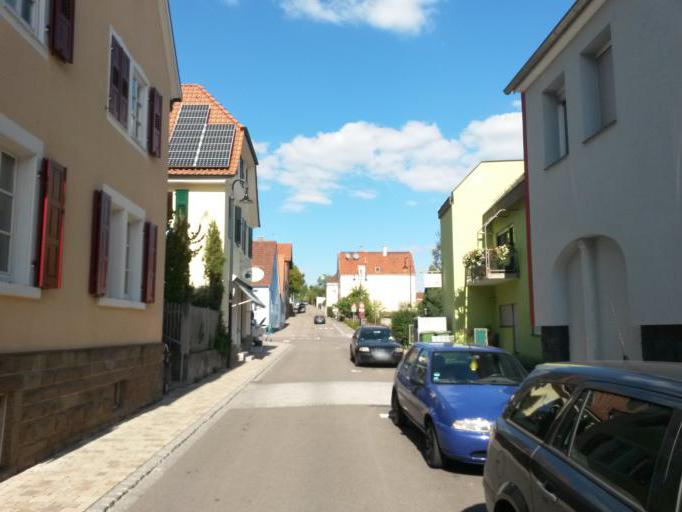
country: DE
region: Baden-Wuerttemberg
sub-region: Karlsruhe Region
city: Muhlacker
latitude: 48.9408
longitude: 8.8409
